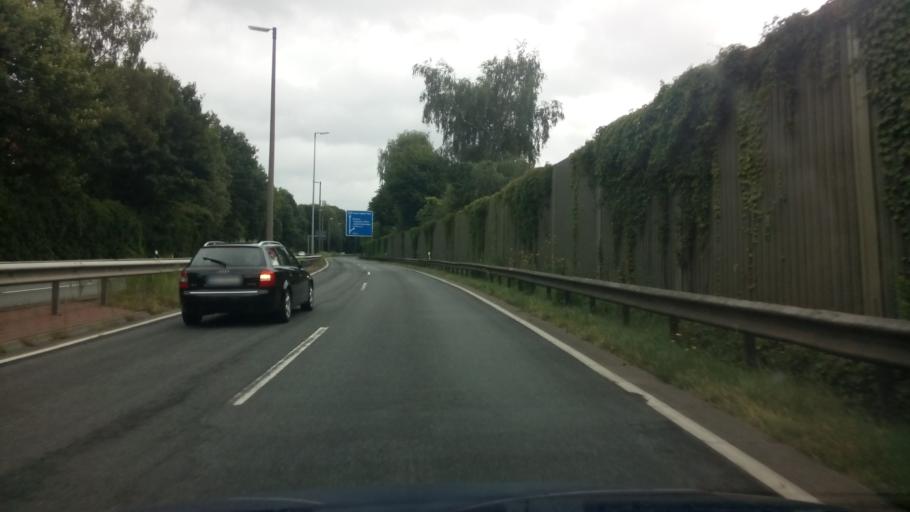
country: DE
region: Lower Saxony
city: Lemwerder
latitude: 53.1808
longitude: 8.6040
